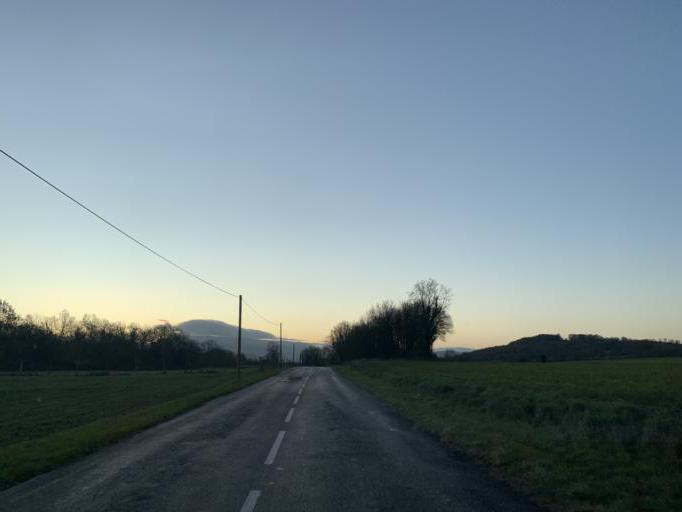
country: FR
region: Rhone-Alpes
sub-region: Departement de l'Ain
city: Virieu-le-Grand
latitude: 45.8002
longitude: 5.6313
